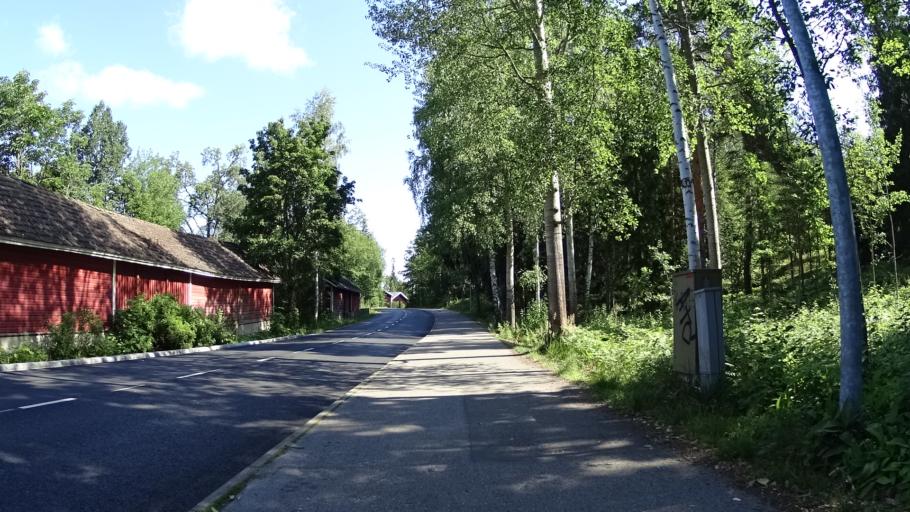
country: FI
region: Uusimaa
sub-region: Helsinki
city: Tuusula
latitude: 60.4106
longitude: 25.0305
